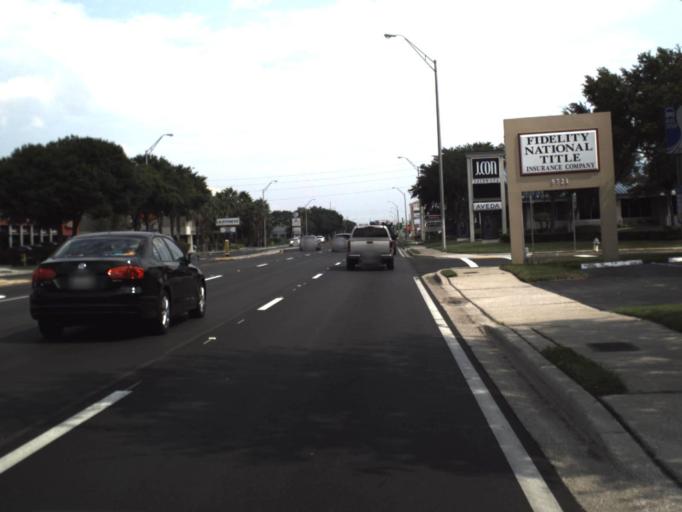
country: US
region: Florida
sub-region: Pinellas County
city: Lealman
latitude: 27.8239
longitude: -82.6385
